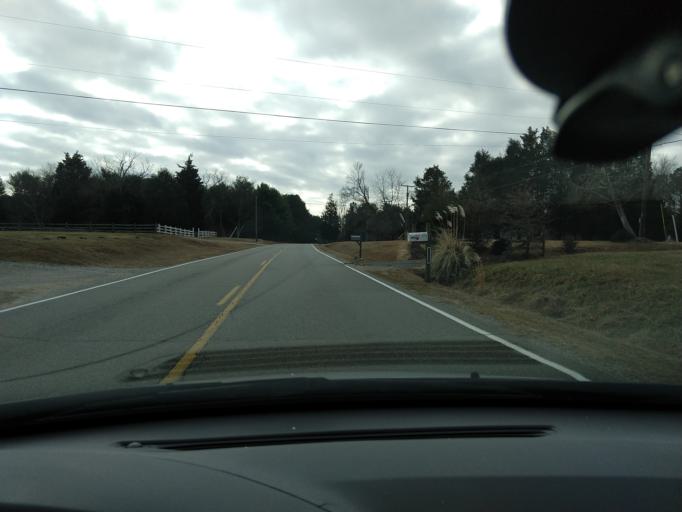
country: US
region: Virginia
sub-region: Henrico County
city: Fort Lee
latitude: 37.4347
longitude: -77.3663
